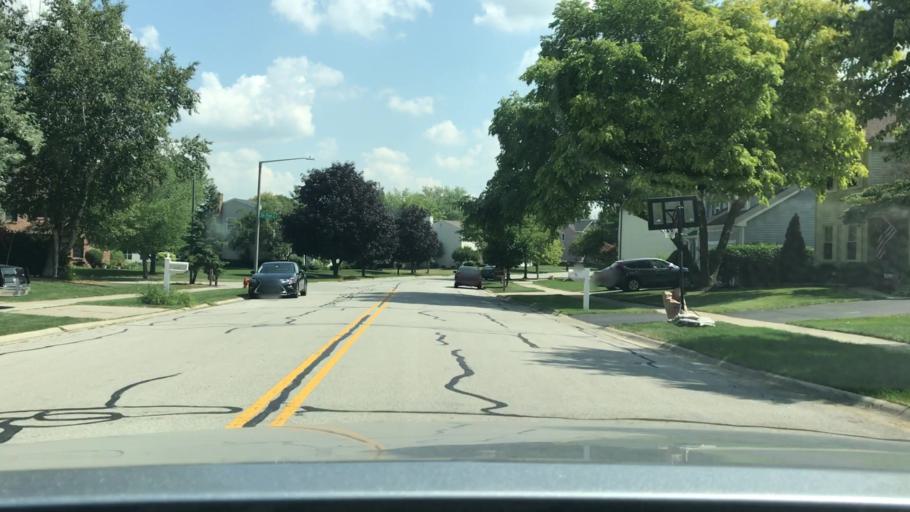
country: US
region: Illinois
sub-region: DuPage County
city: Woodridge
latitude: 41.7432
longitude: -88.1019
